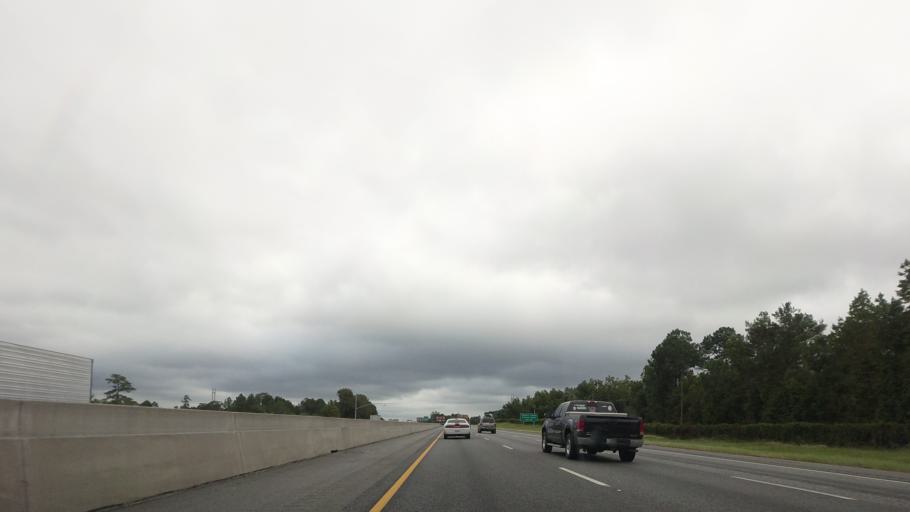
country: US
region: Georgia
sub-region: Lowndes County
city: Remerton
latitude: 30.9059
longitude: -83.3616
